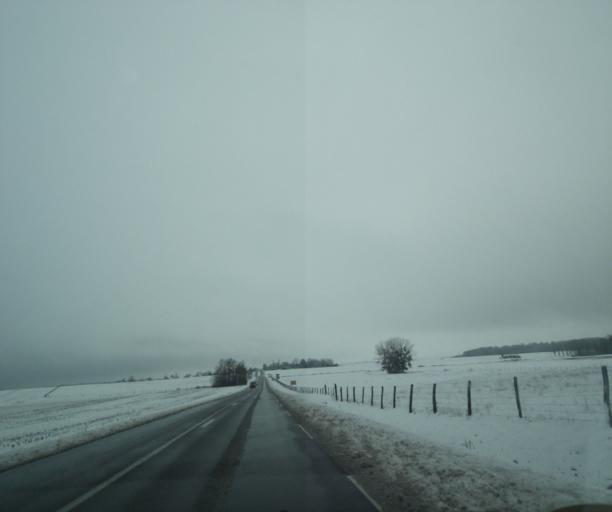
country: FR
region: Champagne-Ardenne
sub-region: Departement de la Haute-Marne
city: Montier-en-Der
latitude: 48.5278
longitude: 4.8150
